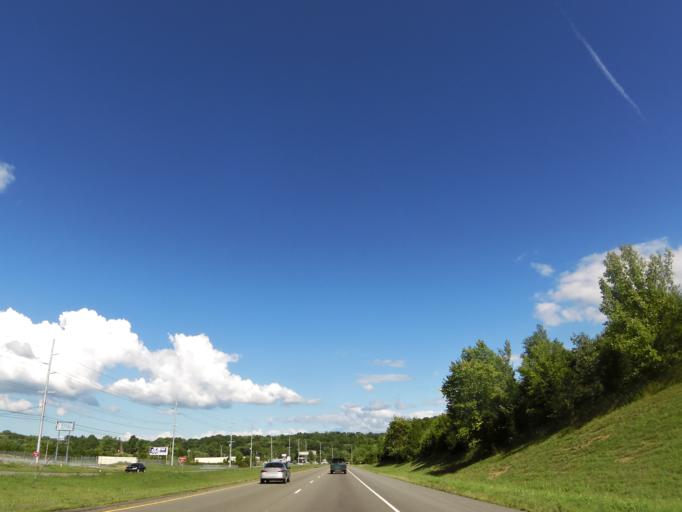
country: US
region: Tennessee
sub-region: Greene County
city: Mosheim
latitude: 36.1863
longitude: -82.9404
